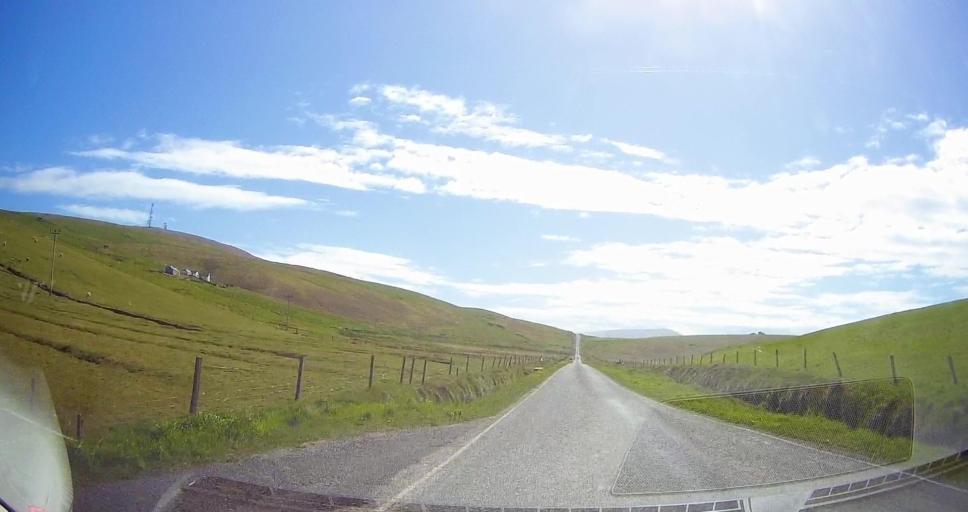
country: GB
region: Scotland
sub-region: Shetland Islands
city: Sandwick
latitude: 59.9677
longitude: -1.3190
